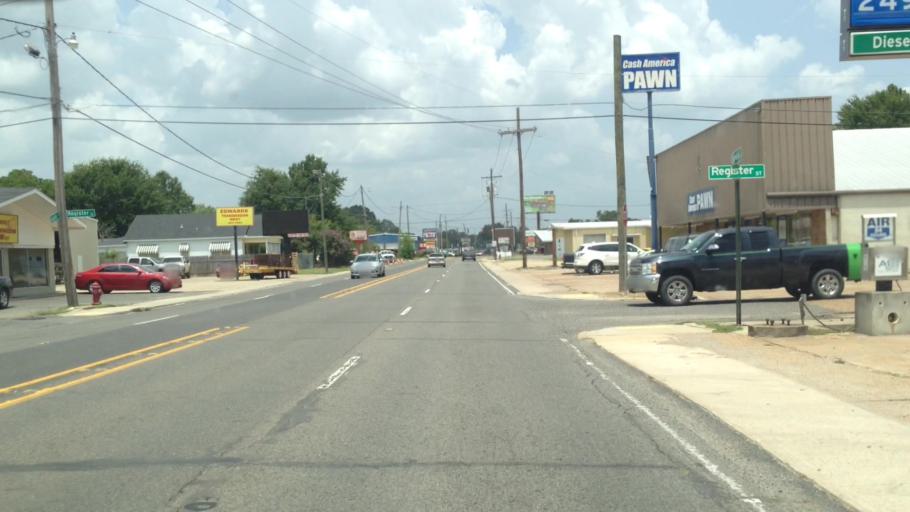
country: US
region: Louisiana
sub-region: Ouachita Parish
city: West Monroe
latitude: 32.5132
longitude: -92.1364
